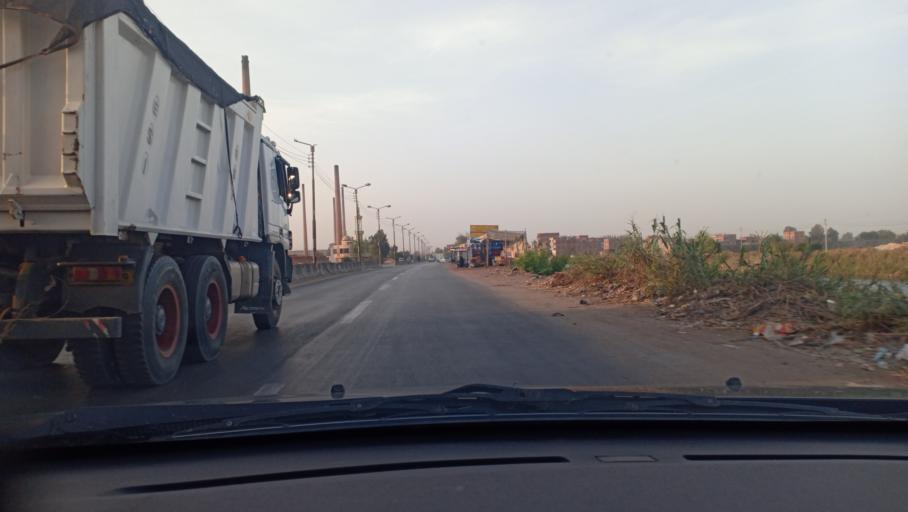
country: EG
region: Muhafazat al Gharbiyah
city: Zifta
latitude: 30.6095
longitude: 31.2755
